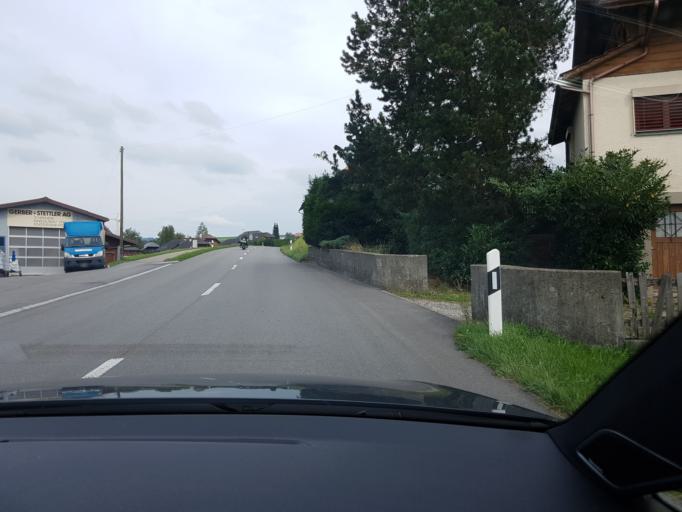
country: CH
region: Bern
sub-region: Thun District
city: Buchholterberg
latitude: 46.7962
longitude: 7.7022
